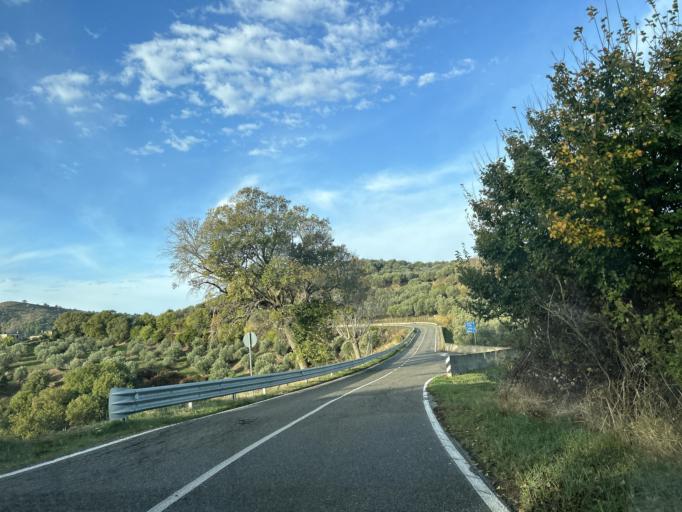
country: IT
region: Calabria
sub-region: Provincia di Catanzaro
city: Montauro
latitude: 38.7630
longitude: 16.5195
